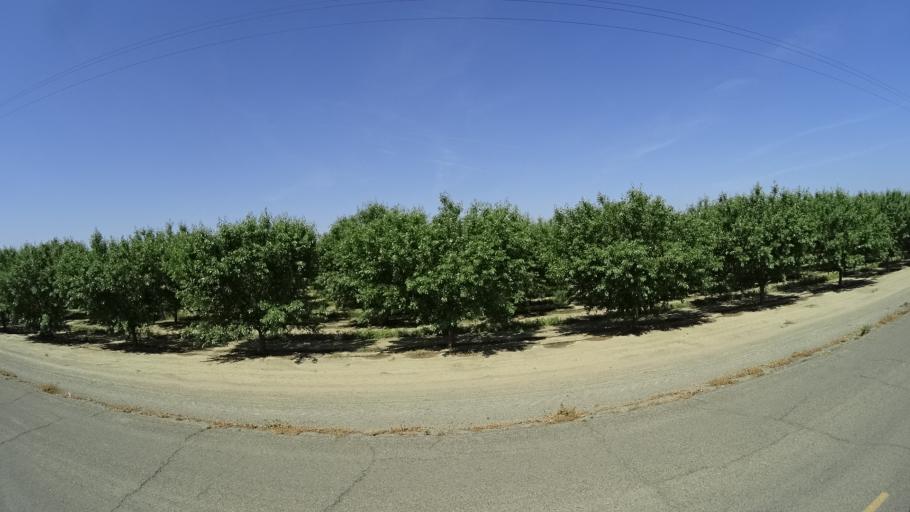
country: US
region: California
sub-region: Kings County
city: Kettleman City
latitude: 36.0556
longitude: -120.0036
